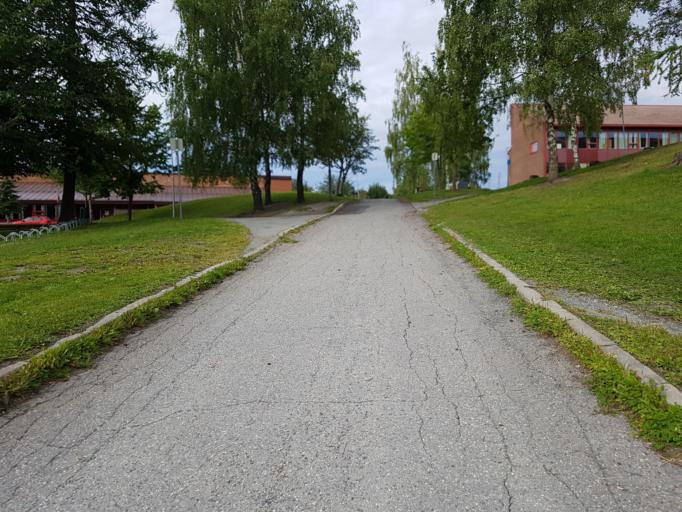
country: NO
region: Sor-Trondelag
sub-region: Trondheim
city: Trondheim
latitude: 63.4003
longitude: 10.4317
